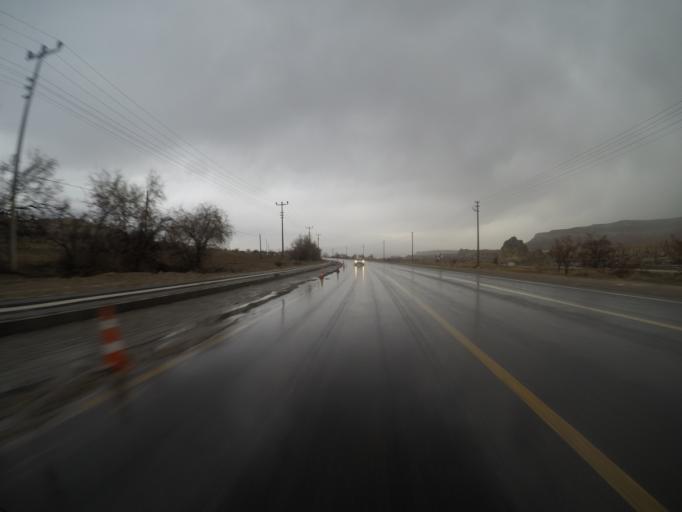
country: TR
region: Nevsehir
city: Goereme
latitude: 38.6533
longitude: 34.8365
